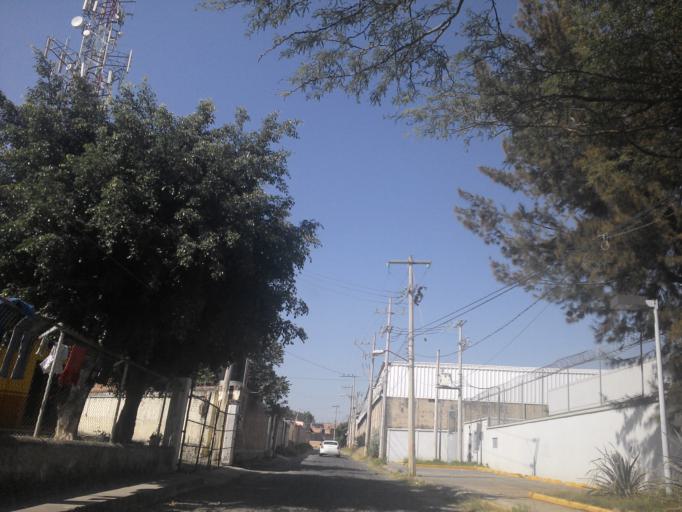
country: MX
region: Jalisco
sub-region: San Pedro Tlaquepaque
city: Paseo del Prado
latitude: 20.5878
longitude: -103.3855
